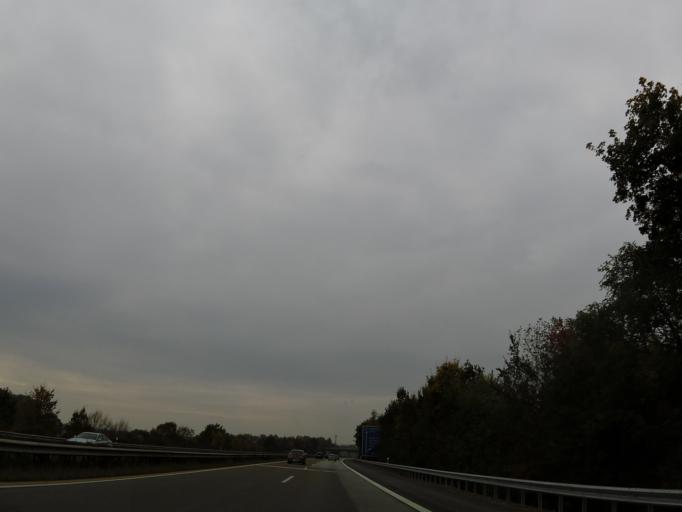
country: DE
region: Rheinland-Pfalz
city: Spiesheim
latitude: 49.8024
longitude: 8.1438
